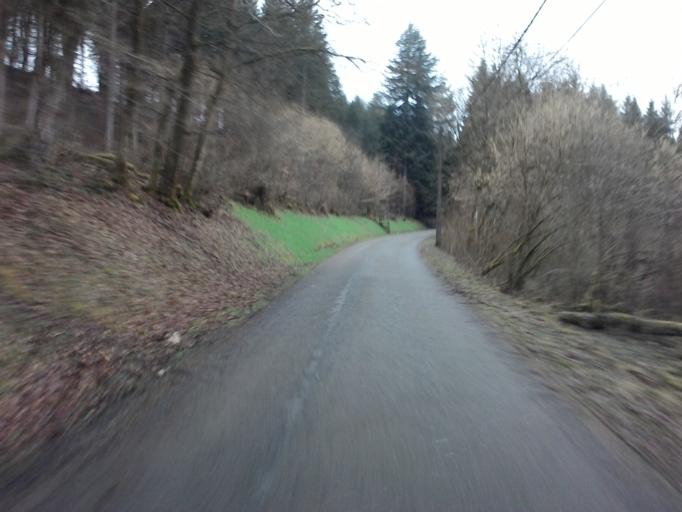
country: BE
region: Wallonia
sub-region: Province de Namur
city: Gedinne
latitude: 50.0284
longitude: 4.8794
